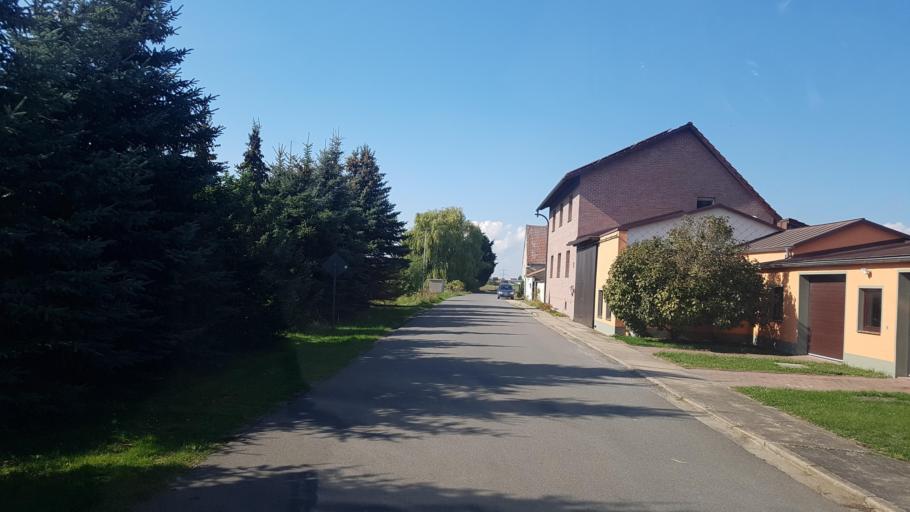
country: DE
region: Brandenburg
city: Ihlow
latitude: 51.8328
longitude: 13.3624
